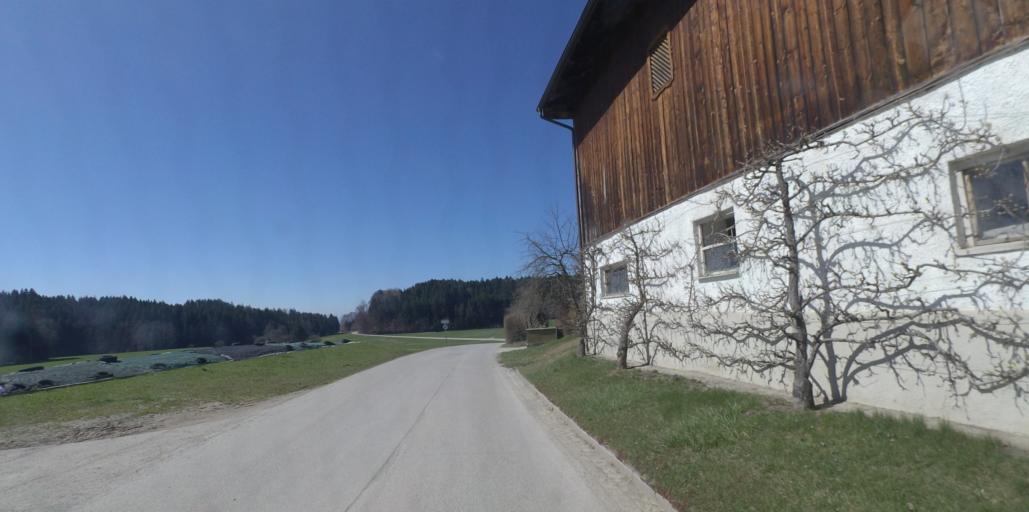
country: DE
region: Bavaria
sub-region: Upper Bavaria
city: Chieming
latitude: 47.8760
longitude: 12.5624
